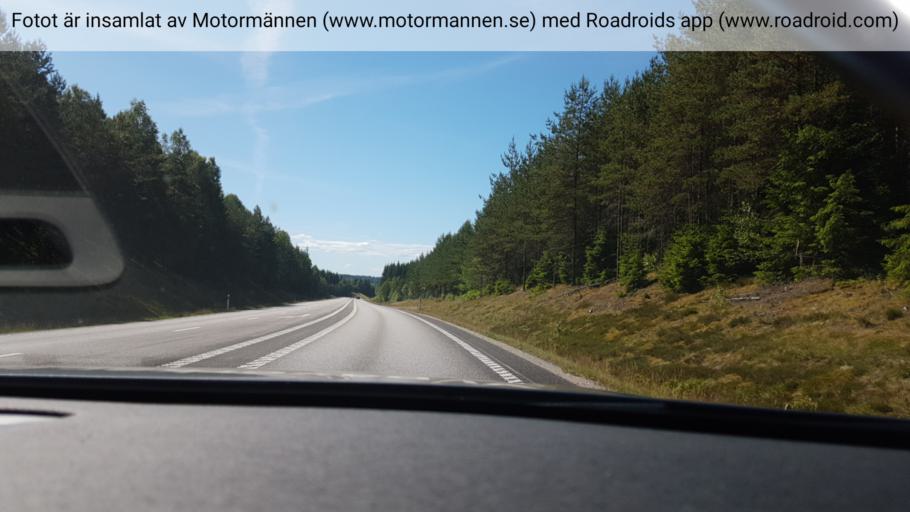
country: SE
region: Vaestra Goetaland
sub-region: Boras Kommun
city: Viskafors
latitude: 57.6099
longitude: 12.8714
